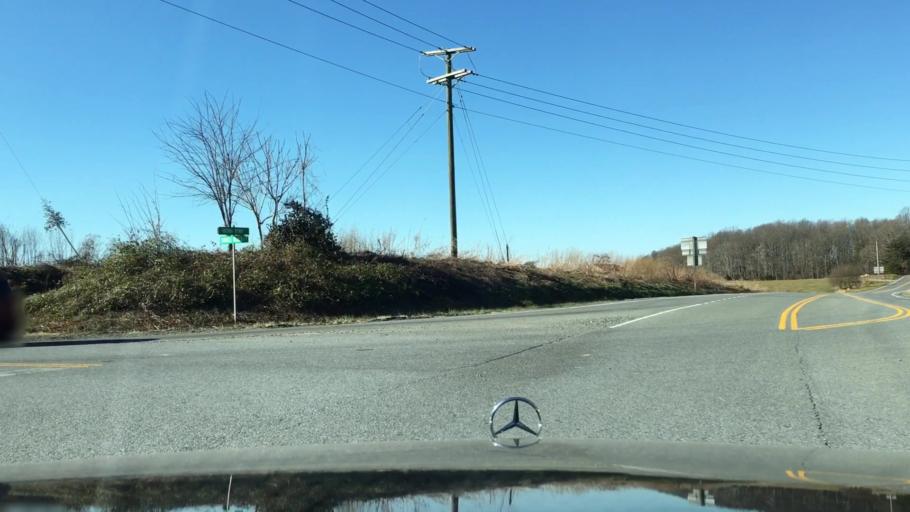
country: US
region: Virginia
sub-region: City of Bedford
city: Bedford
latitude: 37.2237
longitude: -79.4677
